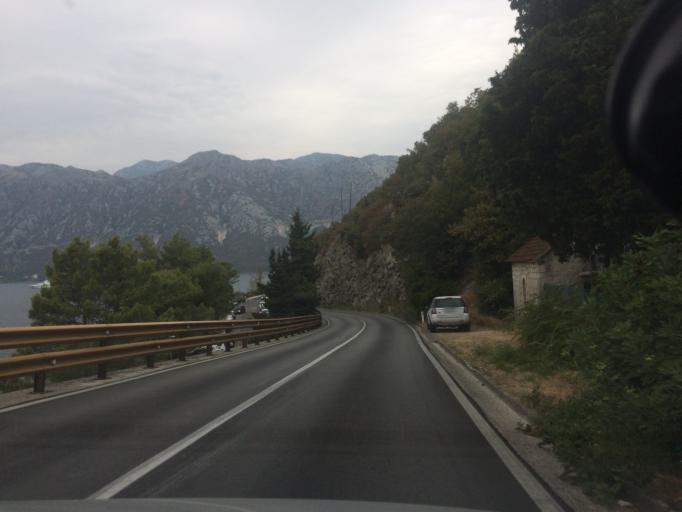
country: ME
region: Kotor
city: Risan
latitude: 42.4889
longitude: 18.6948
